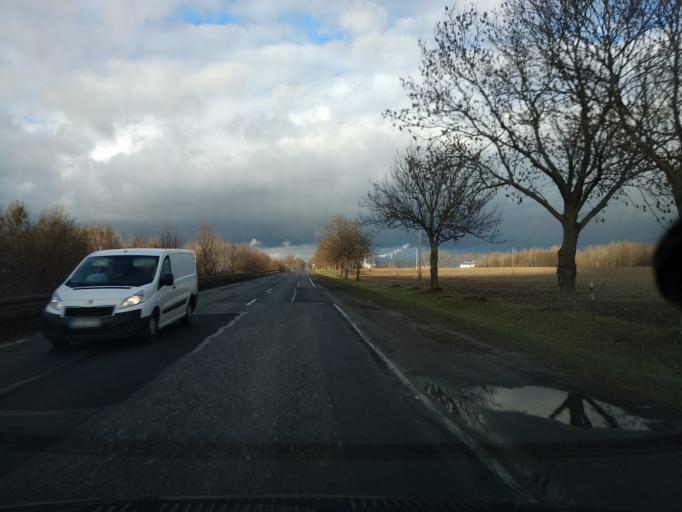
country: PL
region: Greater Poland Voivodeship
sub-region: Konin
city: Konin
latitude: 52.2562
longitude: 18.2688
